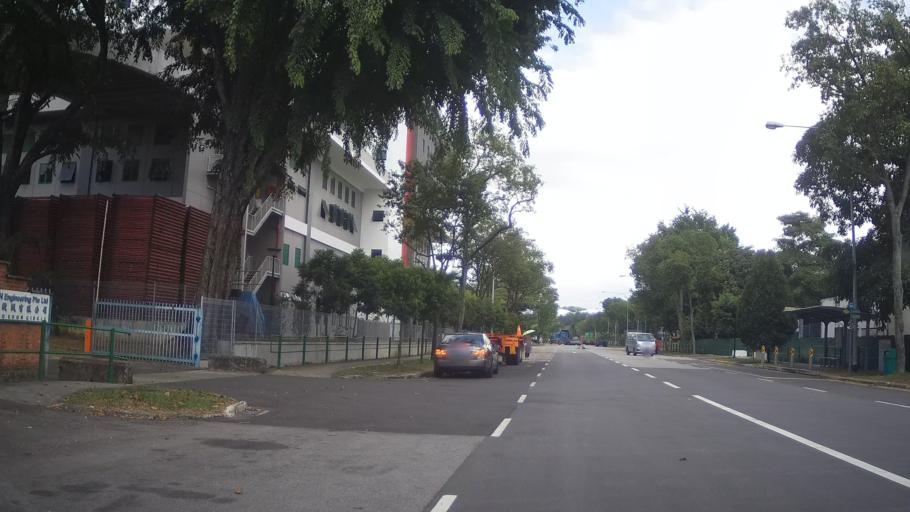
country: MY
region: Johor
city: Johor Bahru
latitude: 1.3237
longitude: 103.6687
